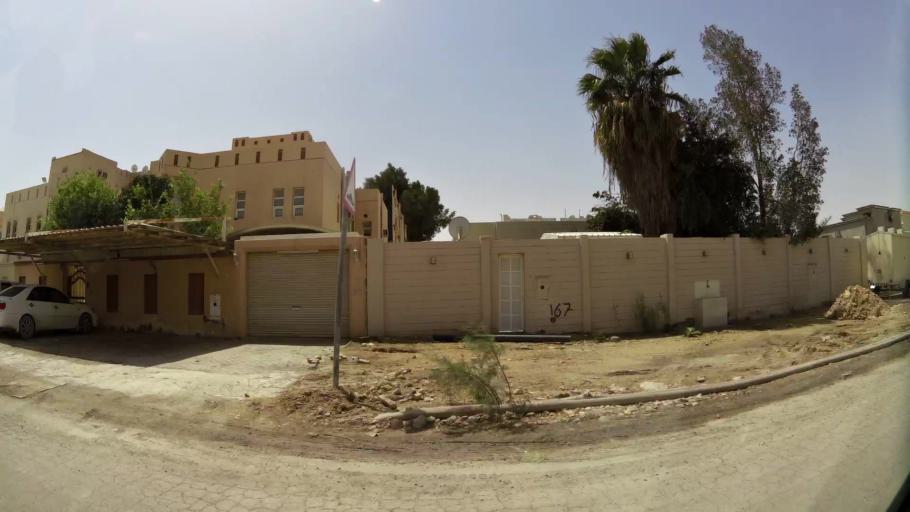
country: QA
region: Baladiyat Umm Salal
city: Umm Salal Muhammad
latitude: 25.3765
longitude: 51.4471
